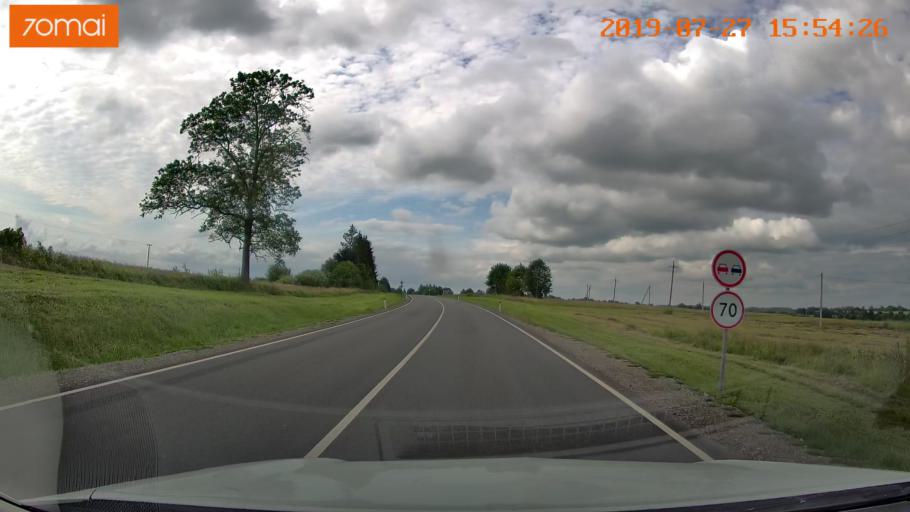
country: RU
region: Kaliningrad
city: Chernyakhovsk
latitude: 54.6076
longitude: 21.9392
